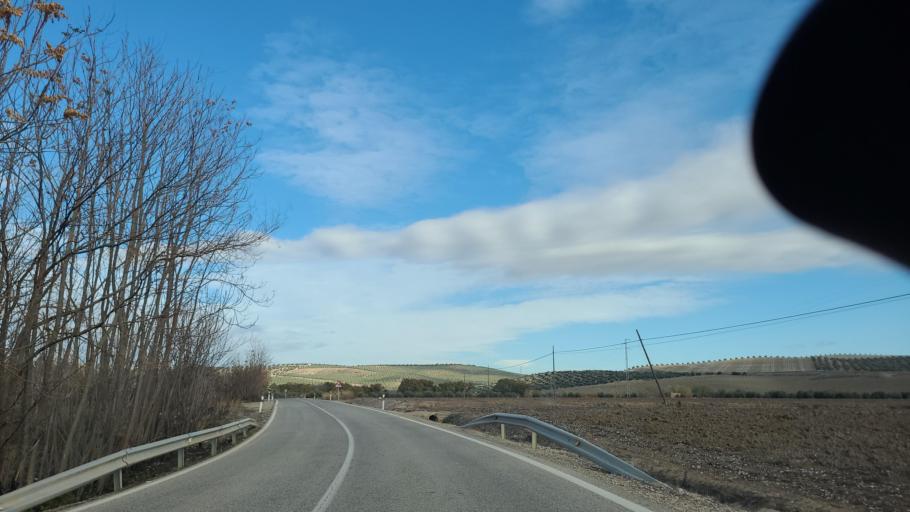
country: ES
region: Andalusia
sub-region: Provincia de Jaen
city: Villanueva de la Reina
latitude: 38.0114
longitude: -3.8945
